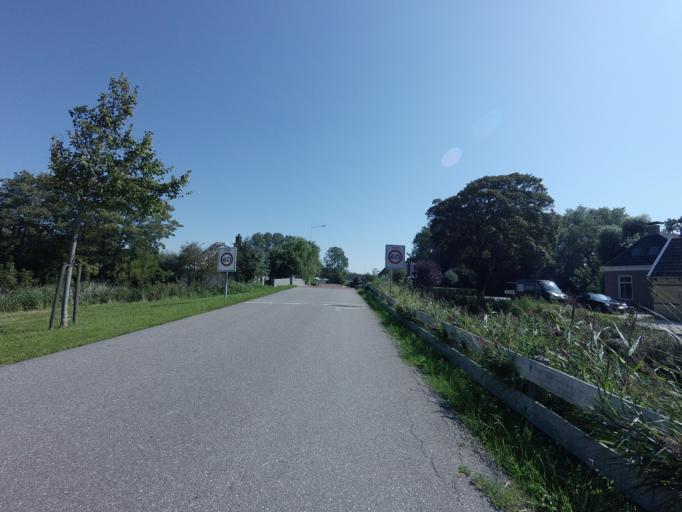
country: NL
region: Friesland
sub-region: Gemeente Dongeradeel
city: Ternaard
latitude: 53.3632
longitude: 5.9684
